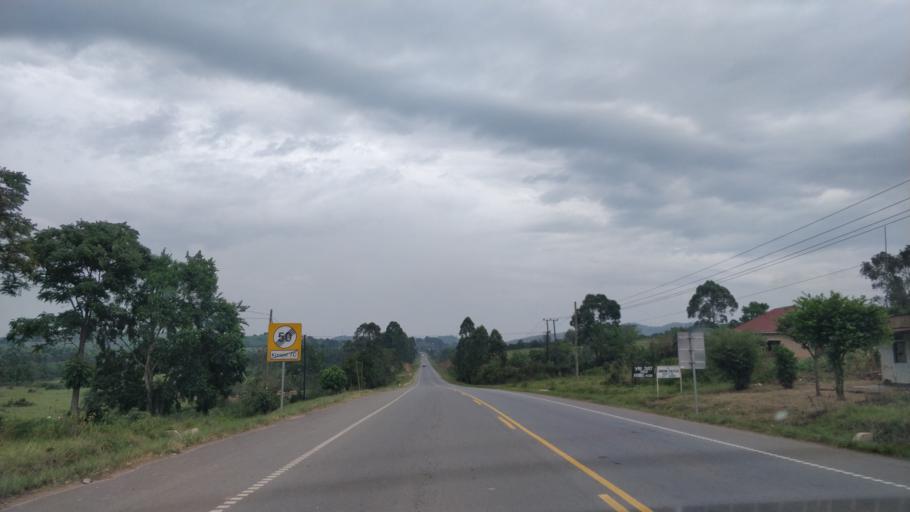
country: UG
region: Western Region
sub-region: Sheema District
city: Kibingo
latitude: -0.6585
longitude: 30.4671
